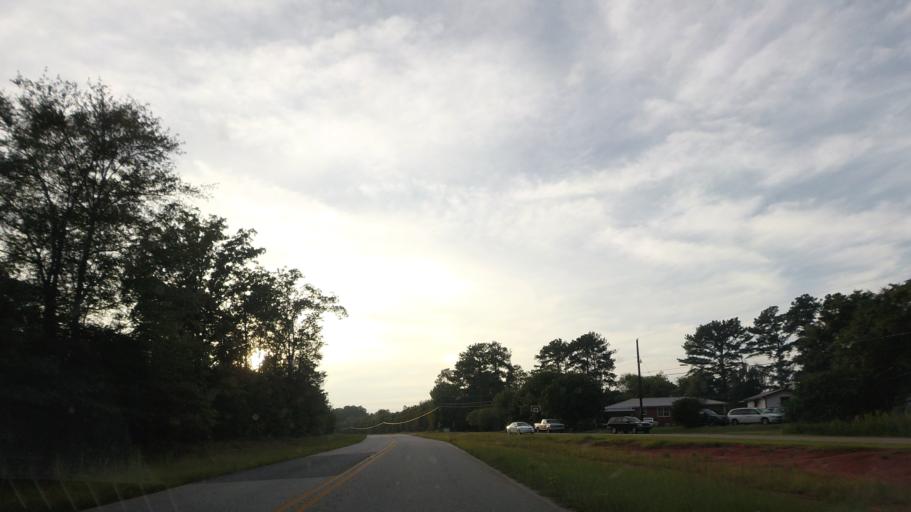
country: US
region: Georgia
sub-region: Bibb County
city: Macon
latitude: 32.8739
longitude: -83.5468
